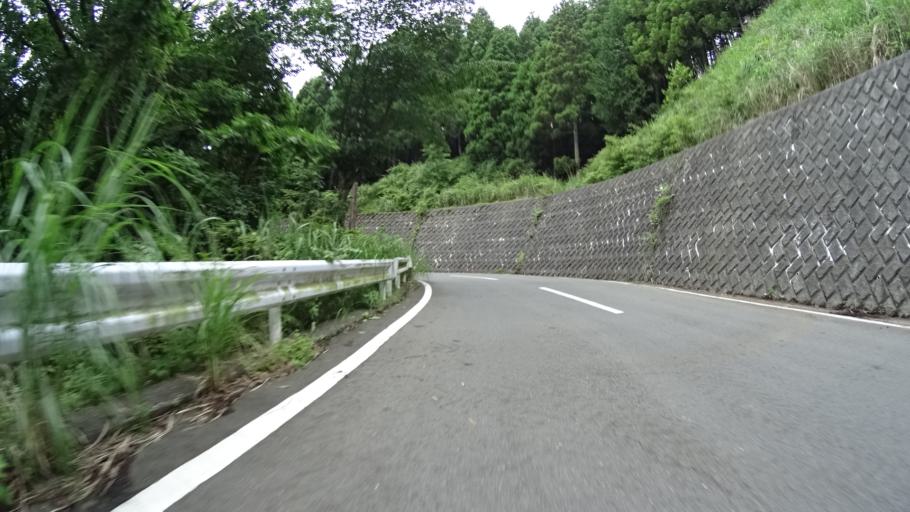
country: JP
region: Kanagawa
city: Hadano
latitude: 35.4321
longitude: 139.2129
